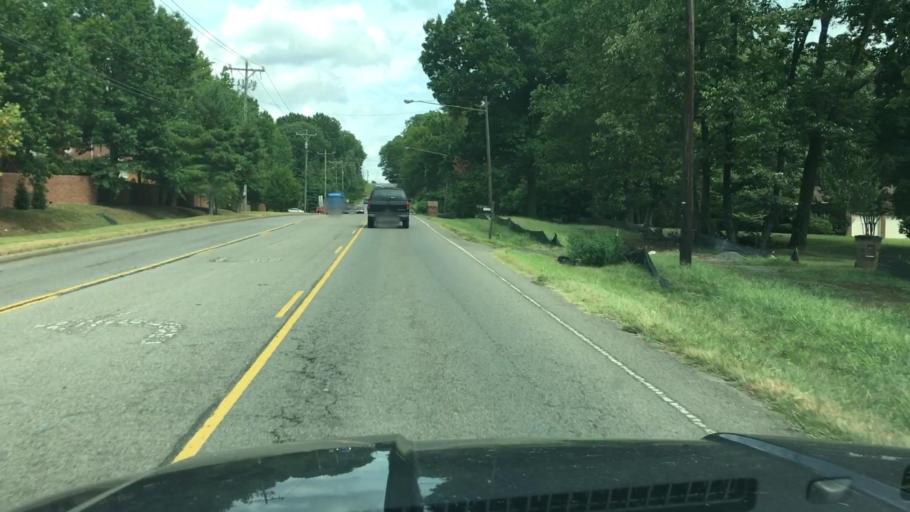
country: US
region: Tennessee
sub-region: Davidson County
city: Oak Hill
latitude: 36.0904
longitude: -86.8148
